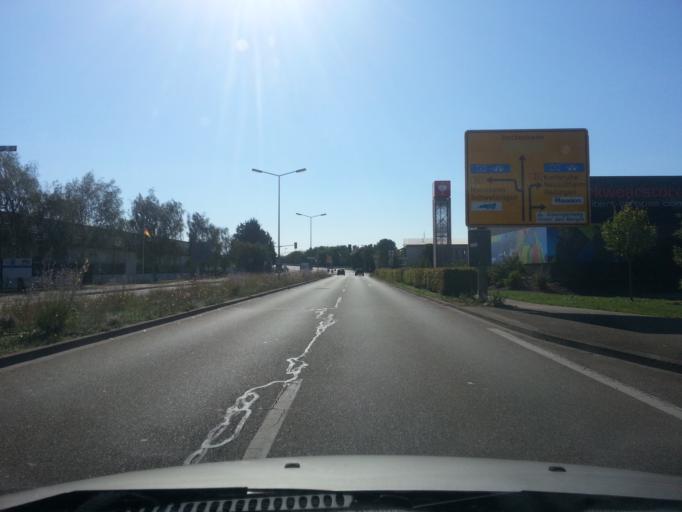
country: DE
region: Baden-Wuerttemberg
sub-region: Karlsruhe Region
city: Hockenheim
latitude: 49.3280
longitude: 8.5380
